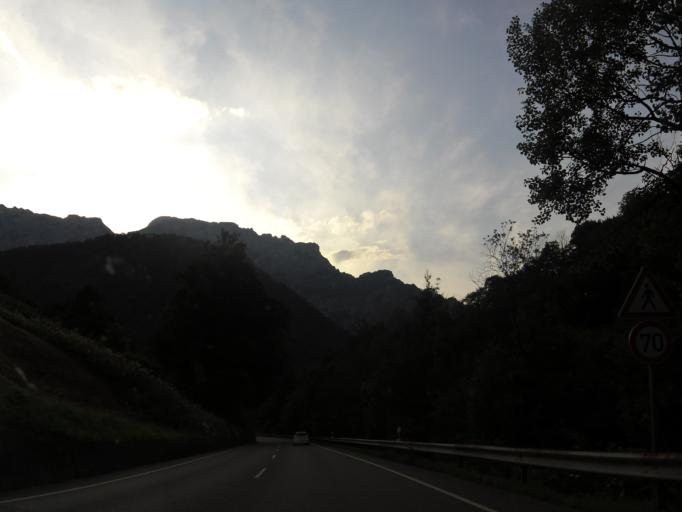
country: DE
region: Bavaria
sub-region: Upper Bavaria
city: Marktschellenberg
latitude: 47.7006
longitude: 13.0430
